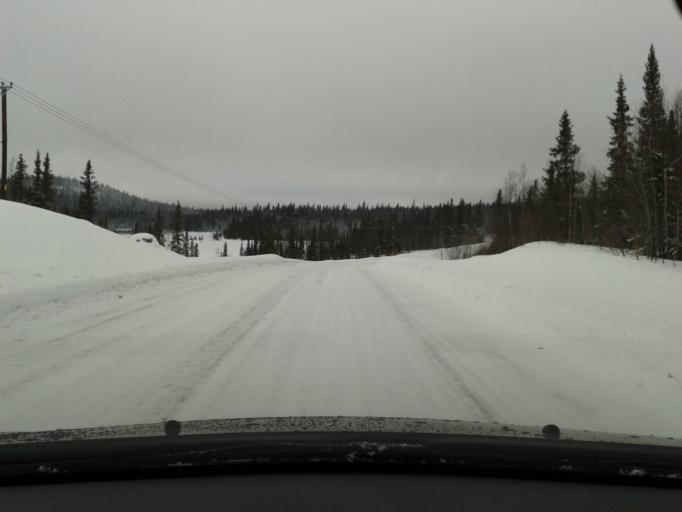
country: SE
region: Vaesterbotten
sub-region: Vilhelmina Kommun
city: Sjoberg
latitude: 65.1861
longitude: 15.9398
